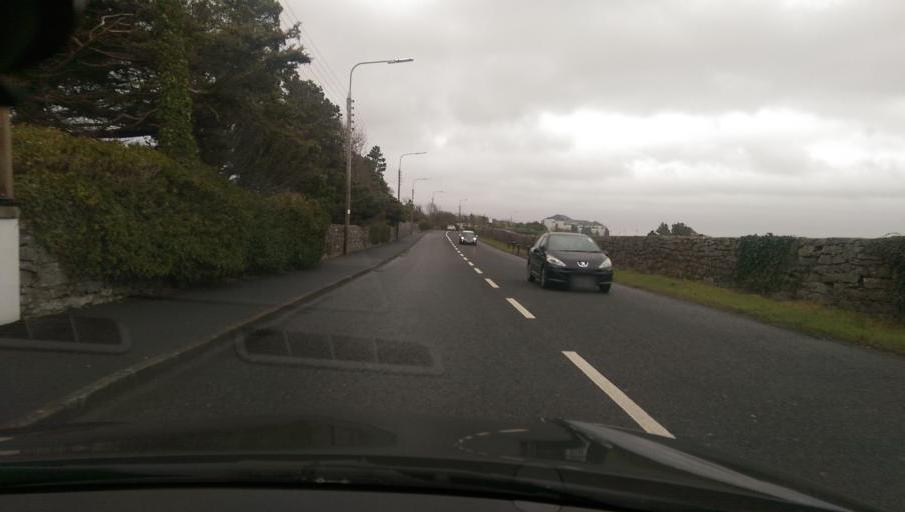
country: IE
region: Connaught
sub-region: County Galway
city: Bearna
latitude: 53.2583
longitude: -9.0994
